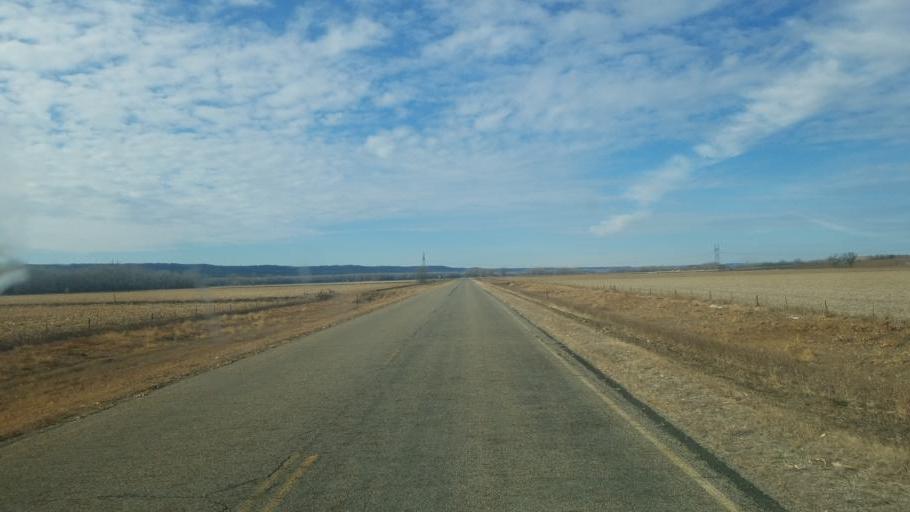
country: US
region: South Dakota
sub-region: Charles Mix County
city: Wagner
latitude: 42.9000
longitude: -98.3125
